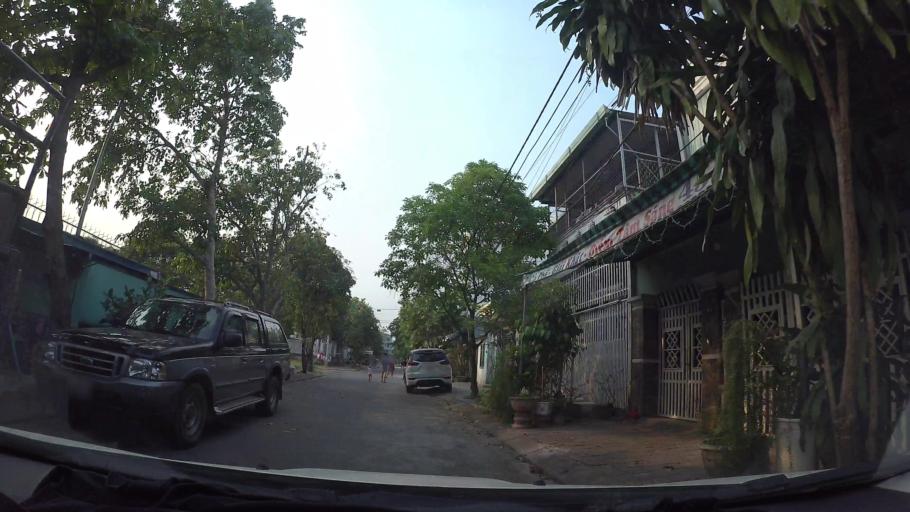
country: VN
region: Da Nang
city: Cam Le
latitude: 16.0181
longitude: 108.1973
